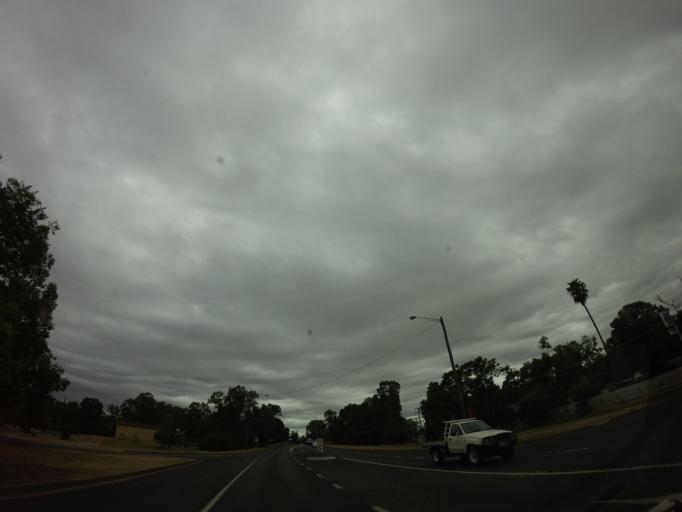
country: AU
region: New South Wales
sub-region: Narrabri
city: Narrabri
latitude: -30.3341
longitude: 149.7712
